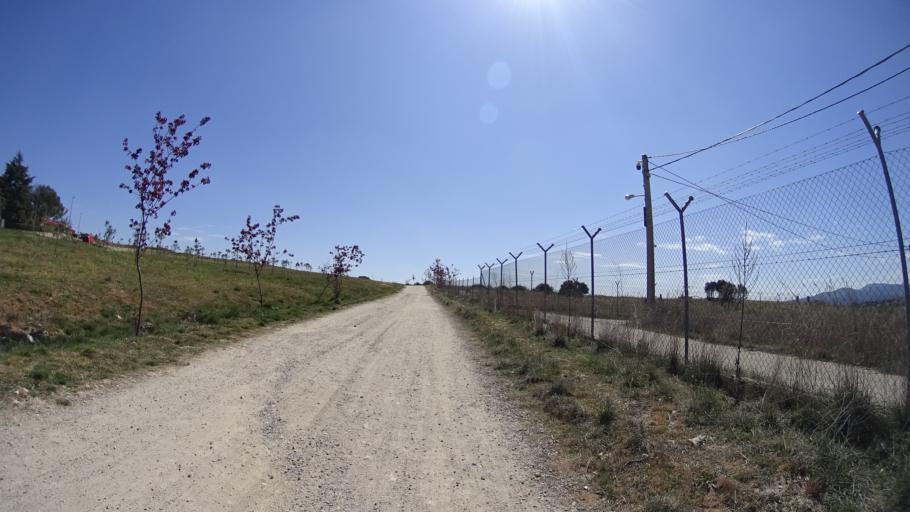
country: ES
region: Madrid
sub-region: Provincia de Madrid
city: Colmenar Viejo
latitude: 40.6712
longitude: -3.7862
